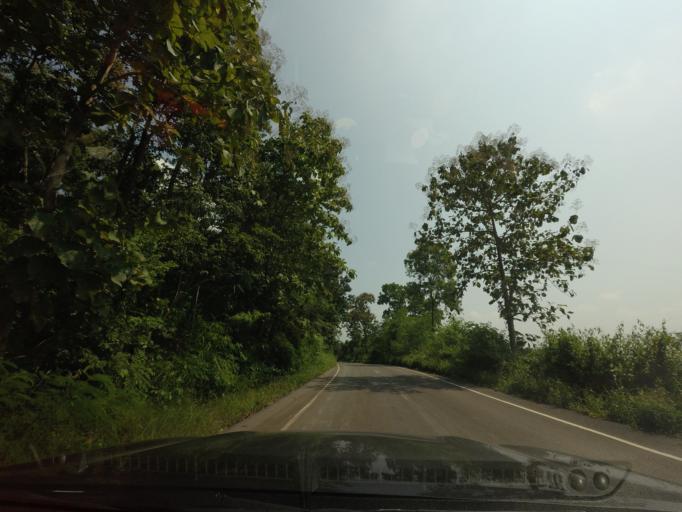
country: TH
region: Nan
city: Nan
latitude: 18.8490
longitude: 100.7802
